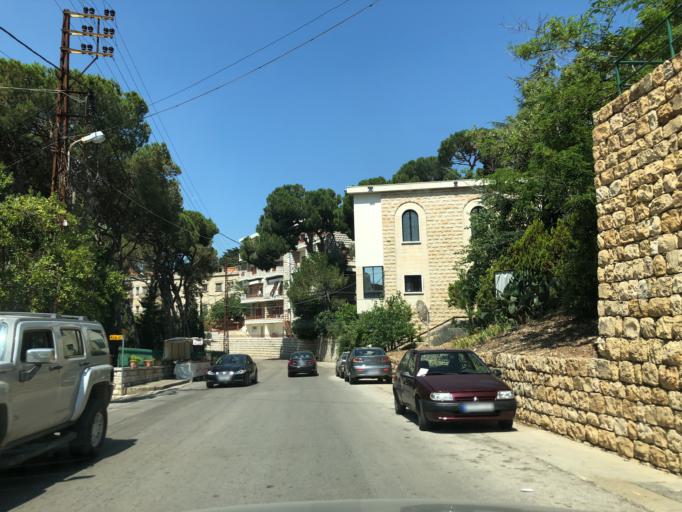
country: LB
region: Mont-Liban
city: Jdaidet el Matn
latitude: 33.8804
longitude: 35.6260
